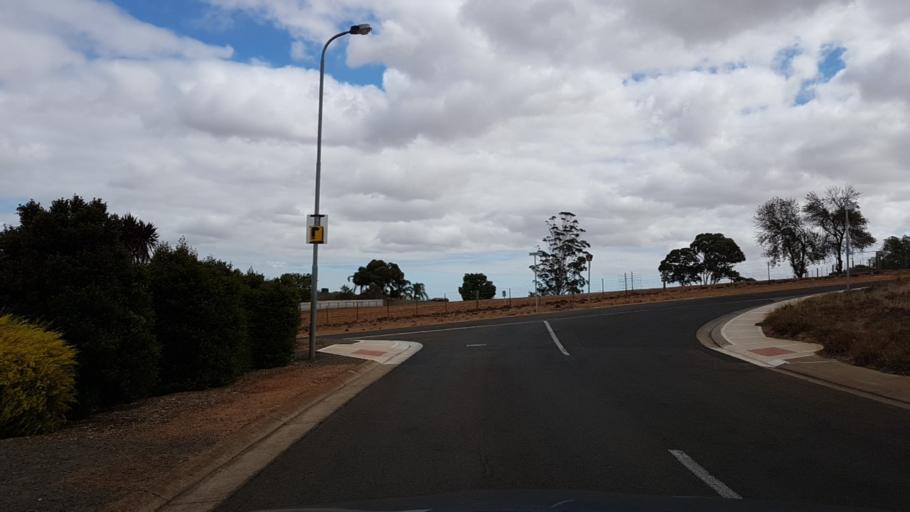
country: AU
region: South Australia
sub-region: Gawler
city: Gawler
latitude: -34.6061
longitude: 138.7577
